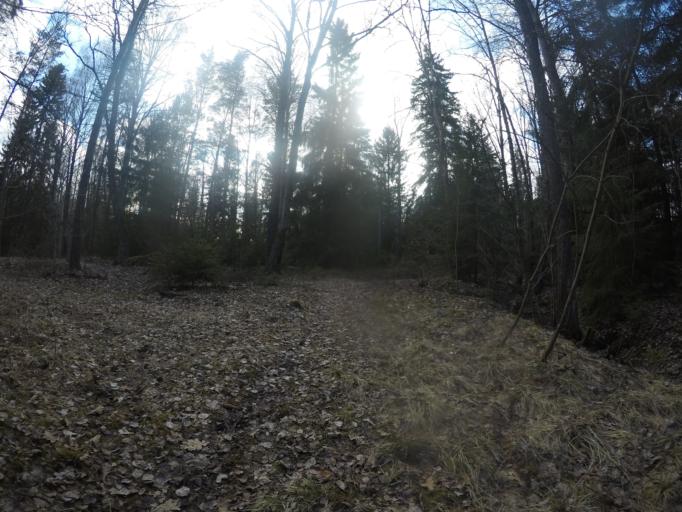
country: SE
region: Soedermanland
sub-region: Eskilstuna Kommun
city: Hallbybrunn
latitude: 59.3914
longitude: 16.4009
